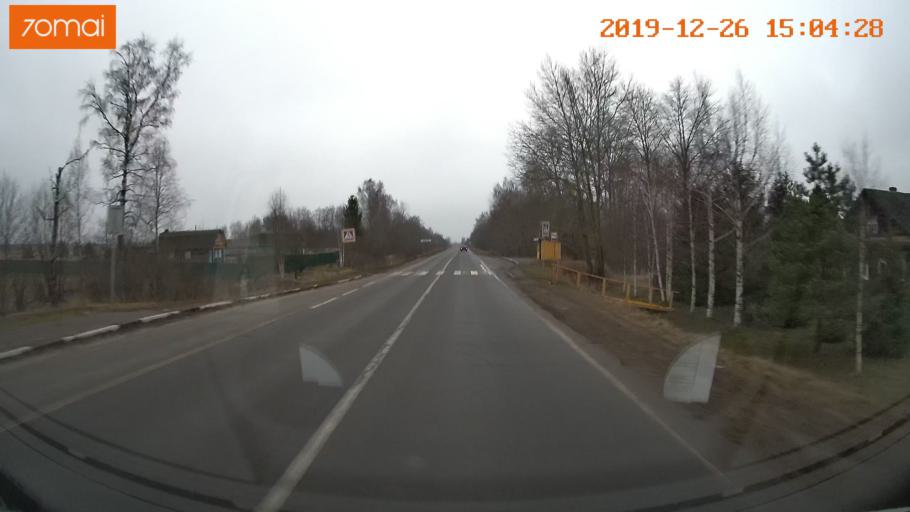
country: RU
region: Jaroslavl
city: Rybinsk
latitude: 58.1995
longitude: 38.8615
